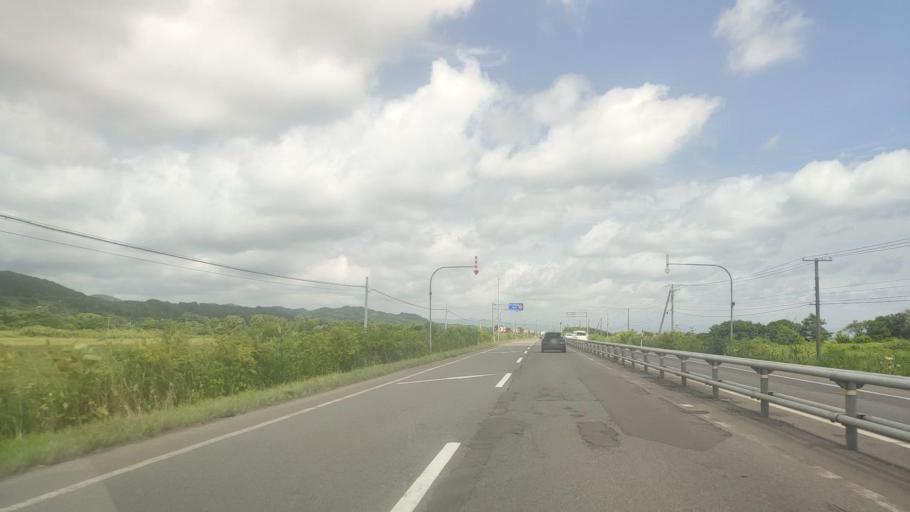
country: JP
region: Hokkaido
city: Niseko Town
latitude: 42.4187
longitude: 140.3116
